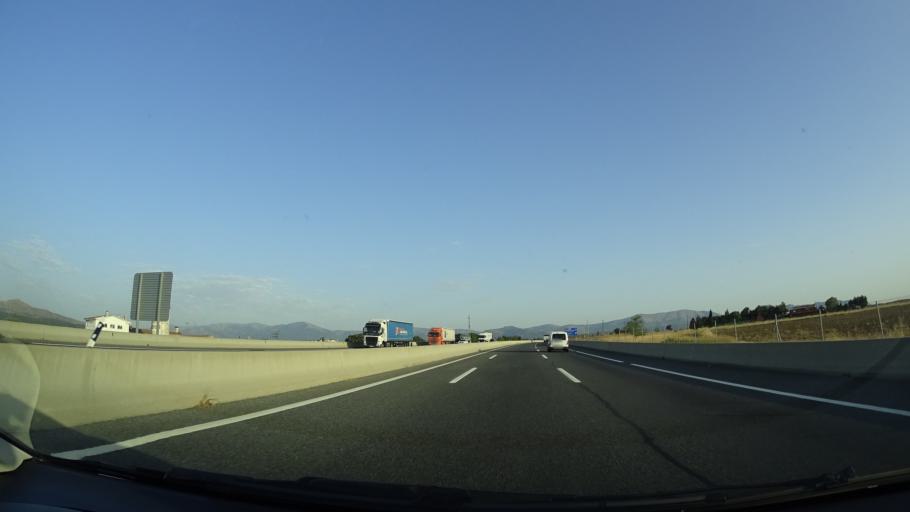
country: ES
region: Madrid
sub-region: Provincia de Madrid
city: Pedrezuela
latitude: 40.7556
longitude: -3.5971
